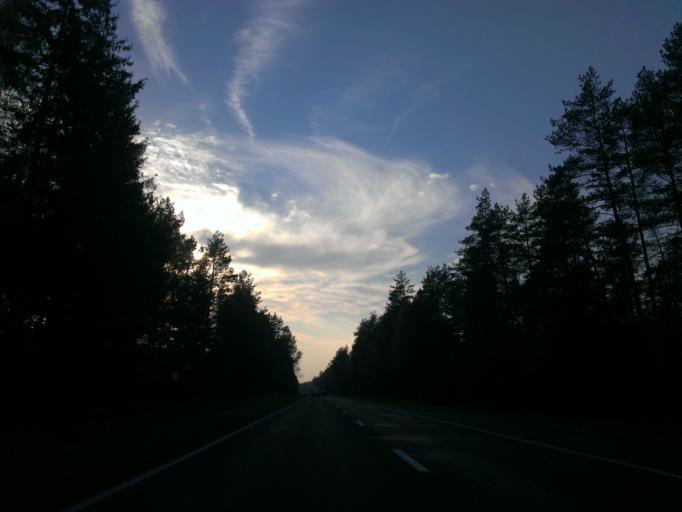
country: LV
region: Incukalns
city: Vangazi
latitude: 57.1056
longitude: 24.5984
